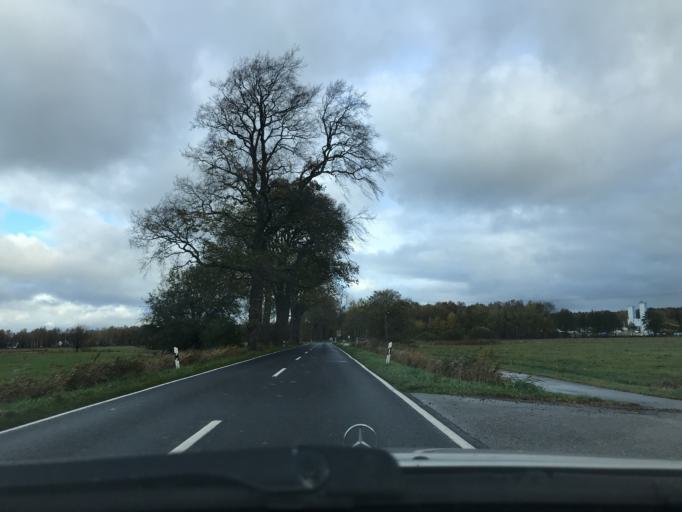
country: DE
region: Mecklenburg-Vorpommern
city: Karlshagen
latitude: 54.0753
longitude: 13.8631
